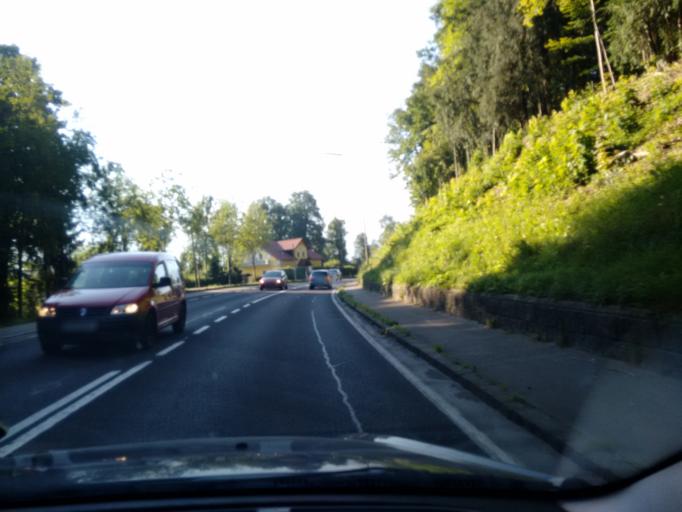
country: AT
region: Upper Austria
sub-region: Politischer Bezirk Gmunden
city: Altmunster
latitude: 47.8890
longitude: 13.7699
